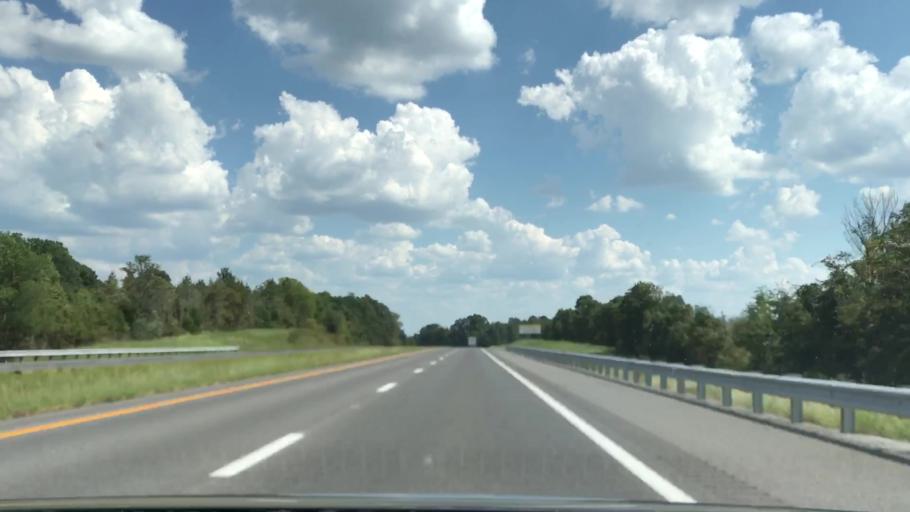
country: US
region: Kentucky
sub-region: Lyon County
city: Eddyville
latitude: 37.1073
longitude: -87.9928
